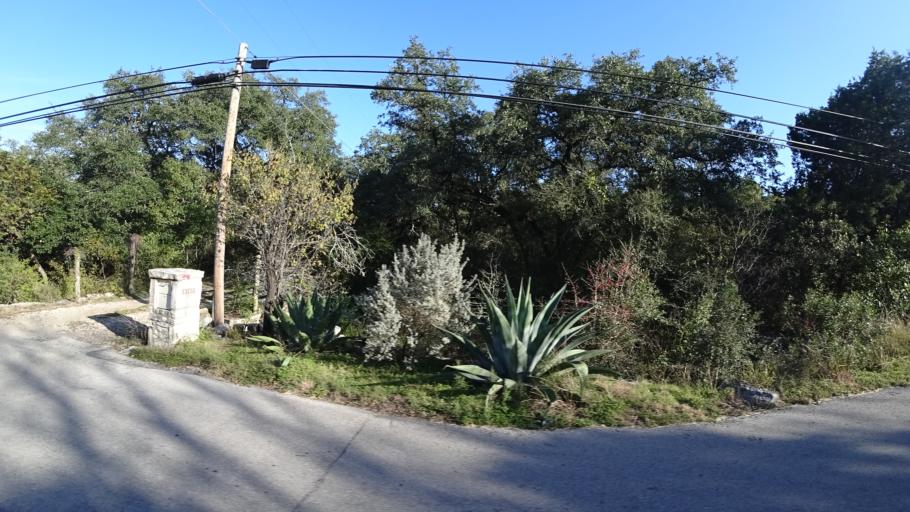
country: US
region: Texas
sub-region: Travis County
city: Barton Creek
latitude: 30.2374
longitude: -97.9098
